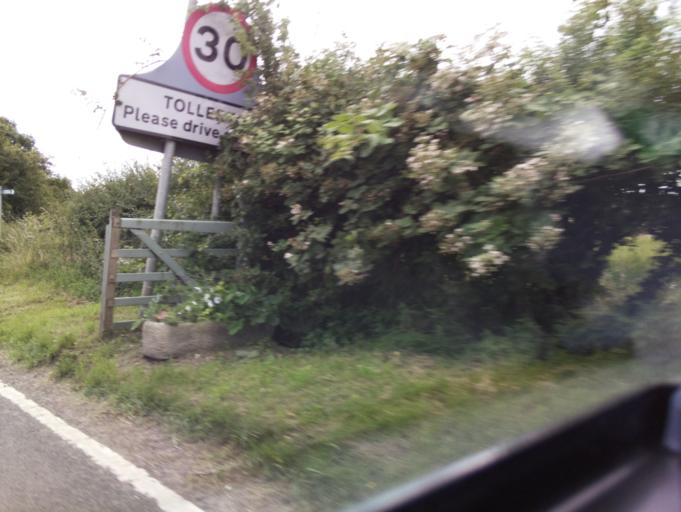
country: GB
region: England
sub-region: Nottinghamshire
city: West Bridgford
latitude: 52.9124
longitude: -1.0843
